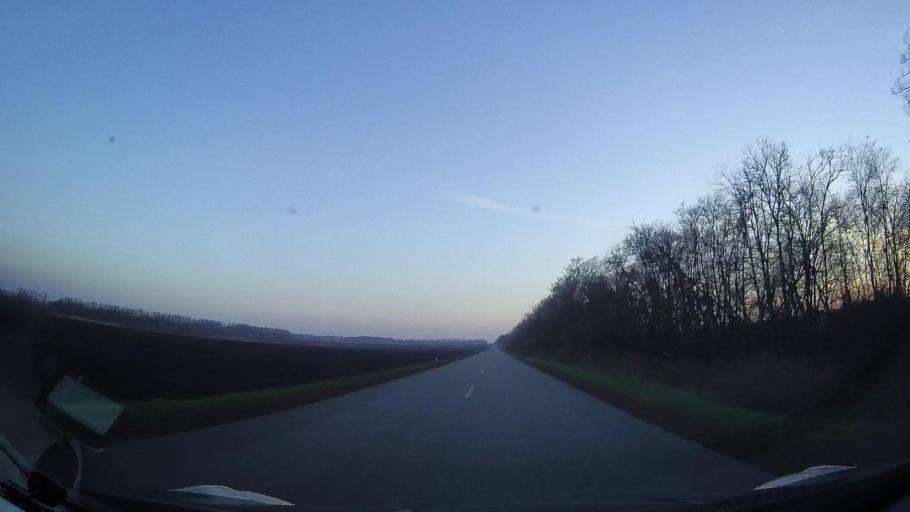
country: RU
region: Rostov
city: Zernograd
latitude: 47.0062
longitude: 40.3915
